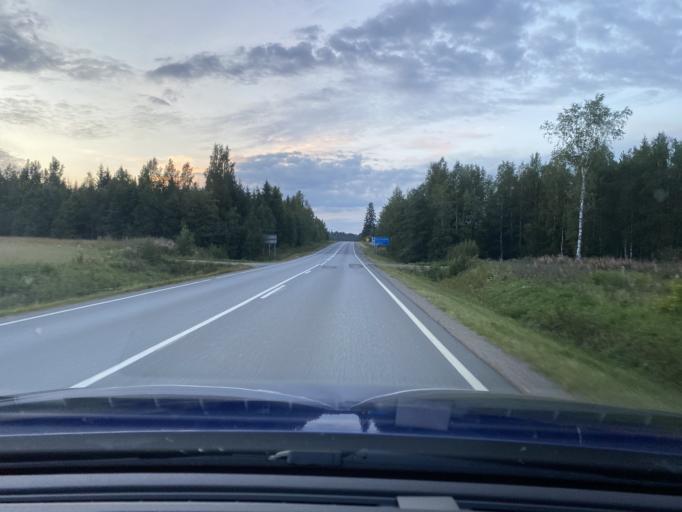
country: FI
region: Satakunta
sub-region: Pohjois-Satakunta
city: Honkajoki
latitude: 62.1025
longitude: 22.2442
